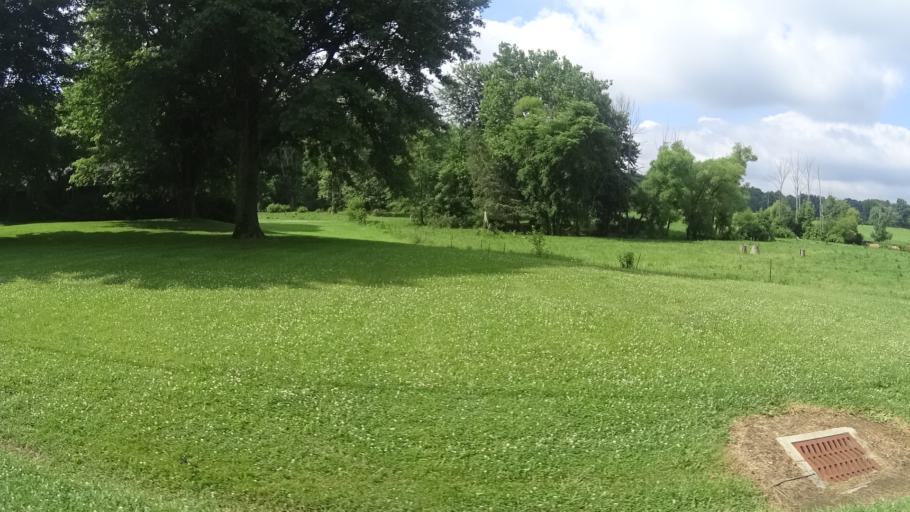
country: US
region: Ohio
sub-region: Huron County
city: Wakeman
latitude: 41.3248
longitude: -82.4279
